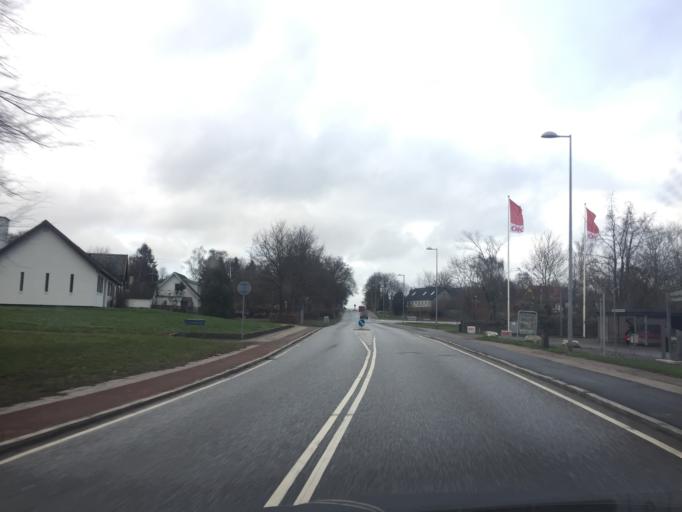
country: DK
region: Zealand
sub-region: Holbaek Kommune
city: Tollose
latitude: 55.6131
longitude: 11.7839
